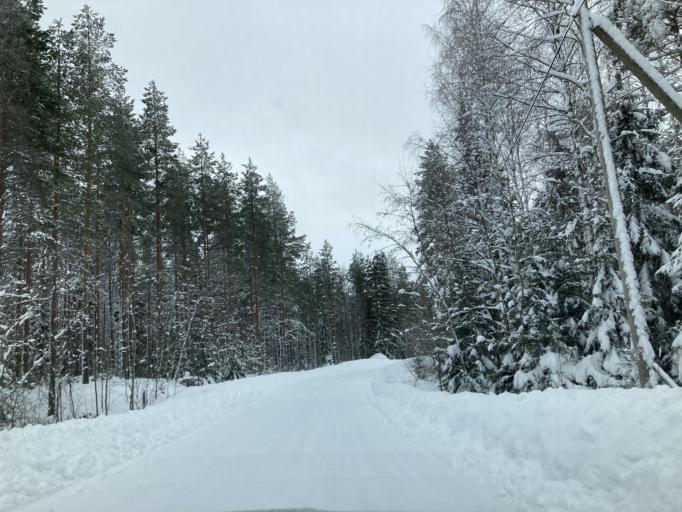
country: FI
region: Central Finland
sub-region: Jaemsae
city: Jaemsae
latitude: 61.8770
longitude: 25.3205
